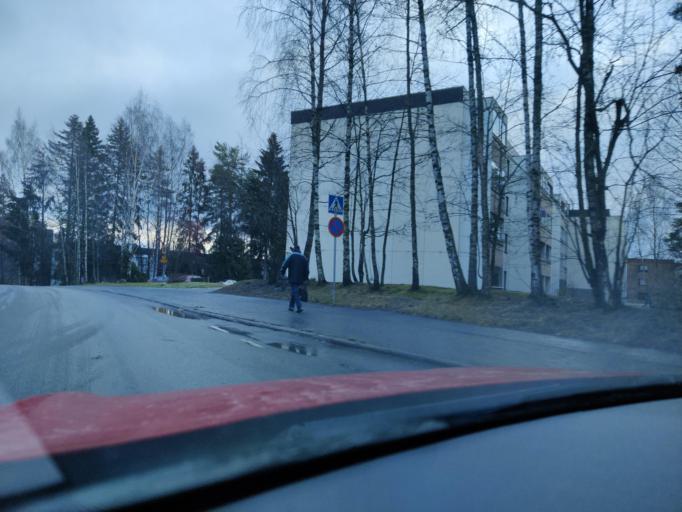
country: FI
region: Pirkanmaa
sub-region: Tampere
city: Nokia
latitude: 61.4635
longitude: 23.4815
